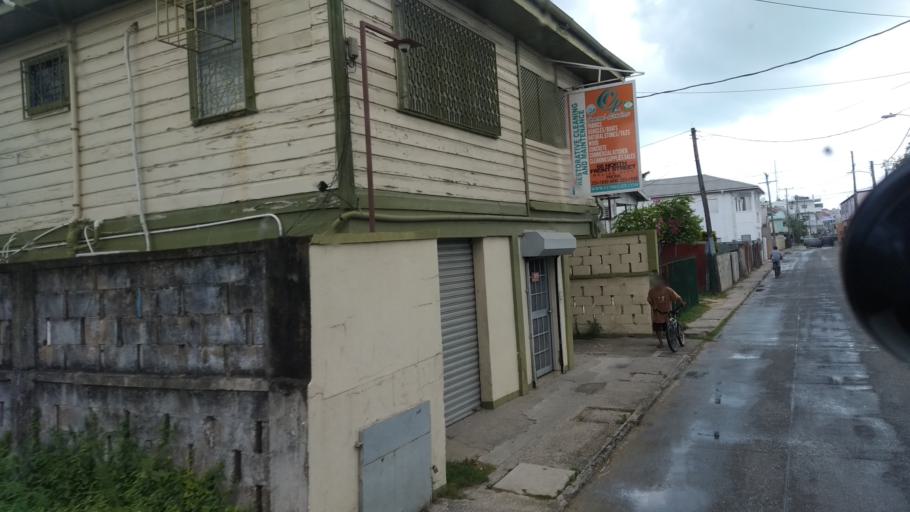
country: BZ
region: Belize
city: Belize City
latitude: 17.4990
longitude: -88.1906
